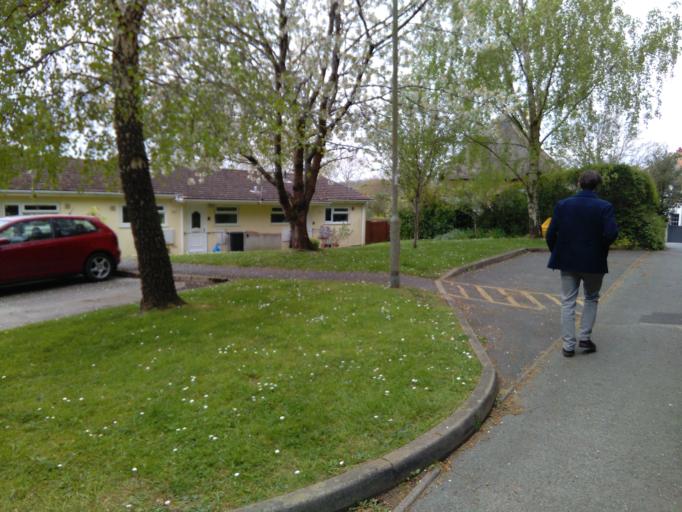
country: GB
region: England
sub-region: Devon
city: Totnes
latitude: 50.4448
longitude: -3.7075
